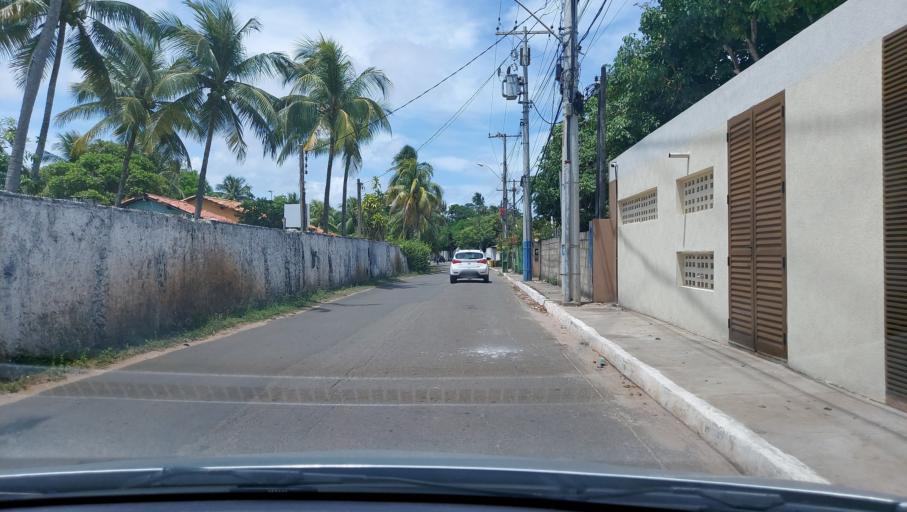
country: BR
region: Bahia
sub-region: Mata De Sao Joao
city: Mata de Sao Joao
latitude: -12.6170
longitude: -38.0441
